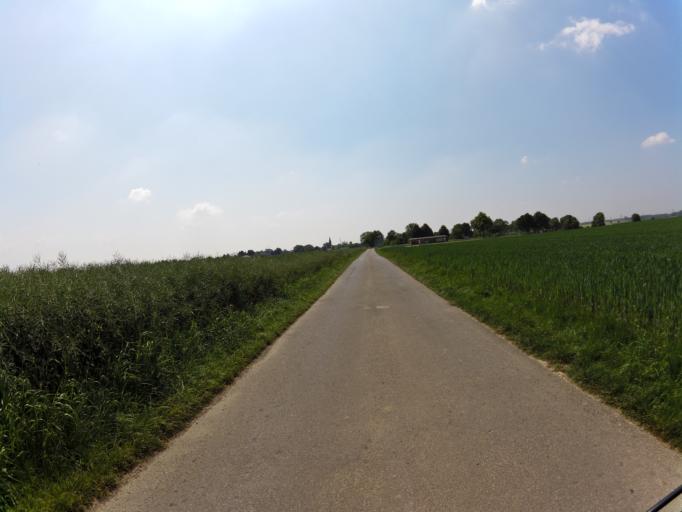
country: DE
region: North Rhine-Westphalia
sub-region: Regierungsbezirk Koln
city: Aldenhoven
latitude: 50.9106
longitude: 6.2651
